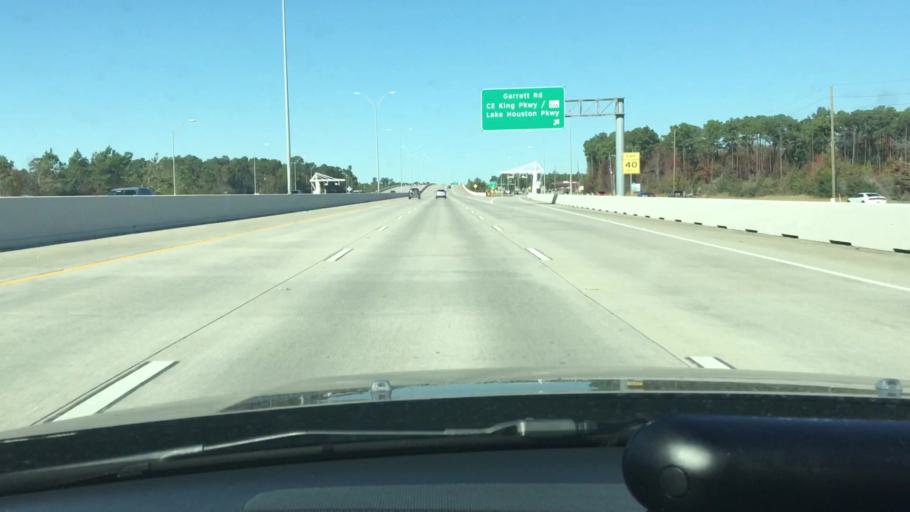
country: US
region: Texas
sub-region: Harris County
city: Sheldon
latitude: 29.8780
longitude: -95.1933
